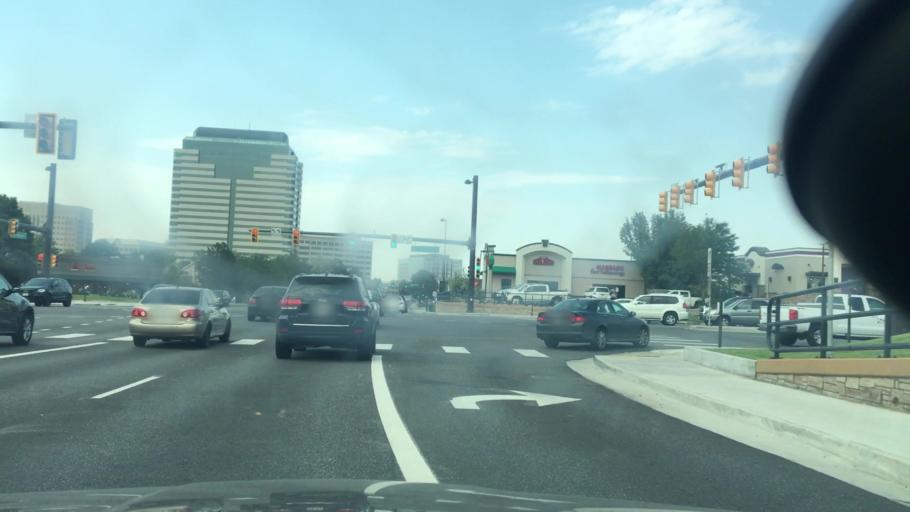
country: US
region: Colorado
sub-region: Arapahoe County
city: Castlewood
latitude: 39.5945
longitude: -104.8888
